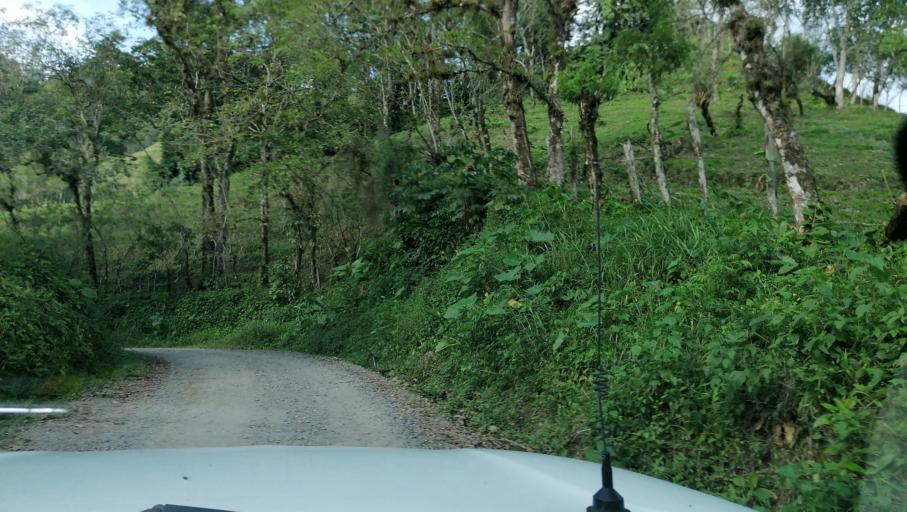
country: MX
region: Chiapas
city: Ostuacan
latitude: 17.4743
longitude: -93.2378
